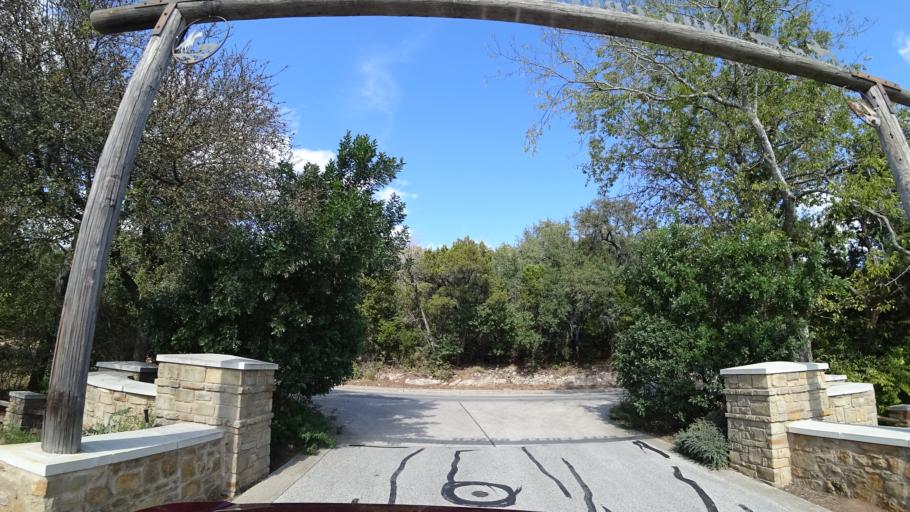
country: US
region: Texas
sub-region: Williamson County
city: Jollyville
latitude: 30.4211
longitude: -97.7964
